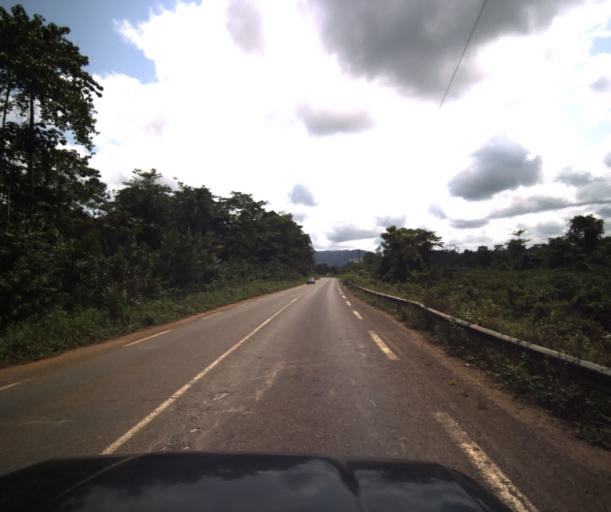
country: CM
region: Centre
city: Eseka
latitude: 3.8857
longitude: 10.7058
